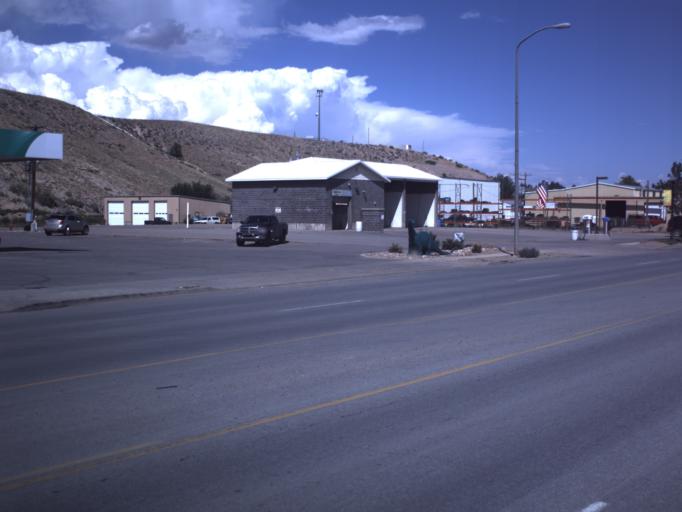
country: US
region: Utah
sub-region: Duchesne County
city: Duchesne
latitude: 40.1634
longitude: -110.4123
